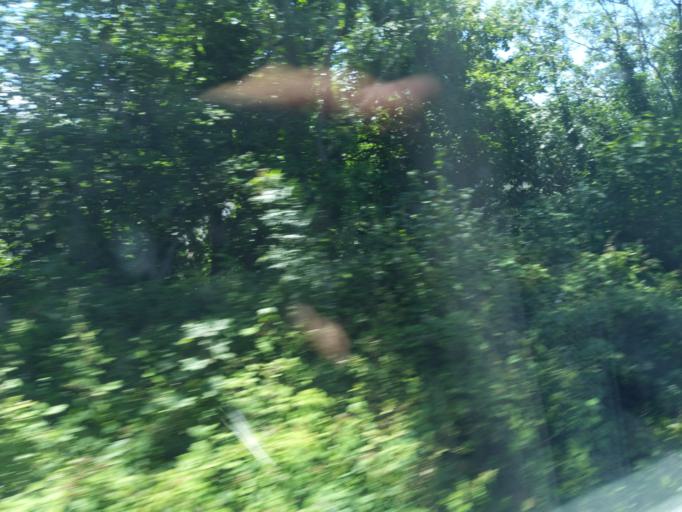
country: GB
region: England
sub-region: Cornwall
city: St Austell
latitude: 50.3419
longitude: -4.7967
